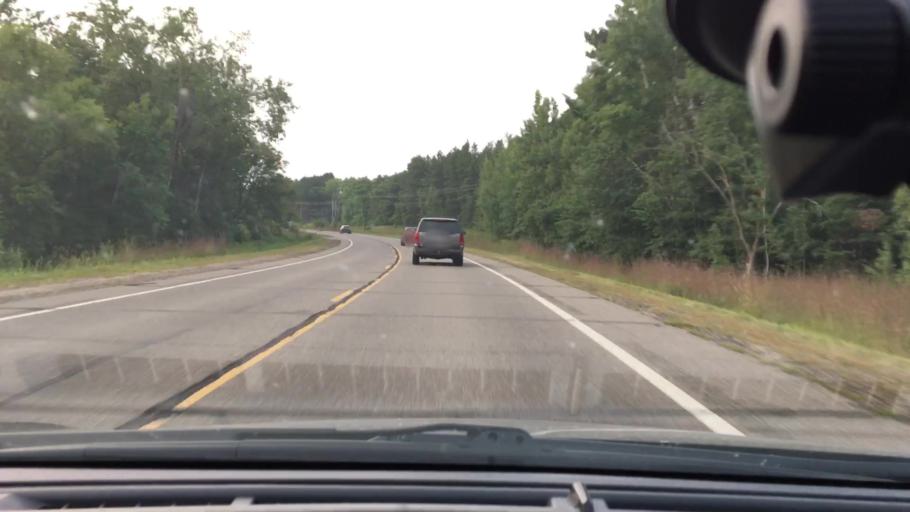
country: US
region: Minnesota
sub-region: Crow Wing County
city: Crosby
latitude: 46.4529
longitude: -93.8795
